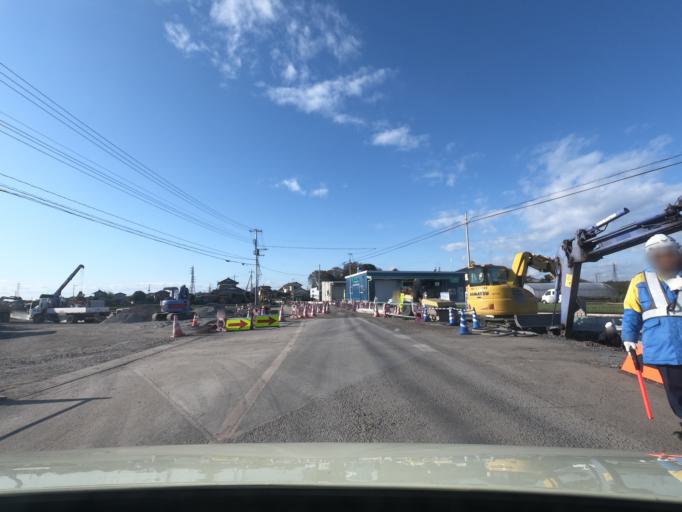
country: JP
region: Ibaraki
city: Koga
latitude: 36.2388
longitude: 139.7504
